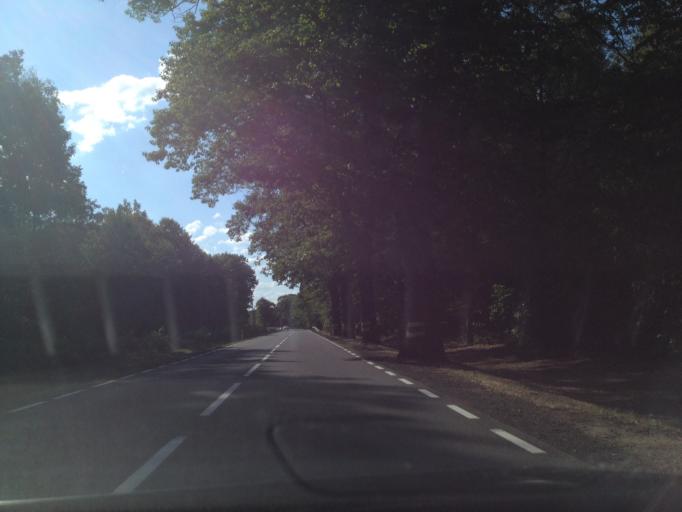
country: PL
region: Lubusz
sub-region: Powiat zarski
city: Lipinki Luzyckie
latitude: 51.6357
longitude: 14.9242
